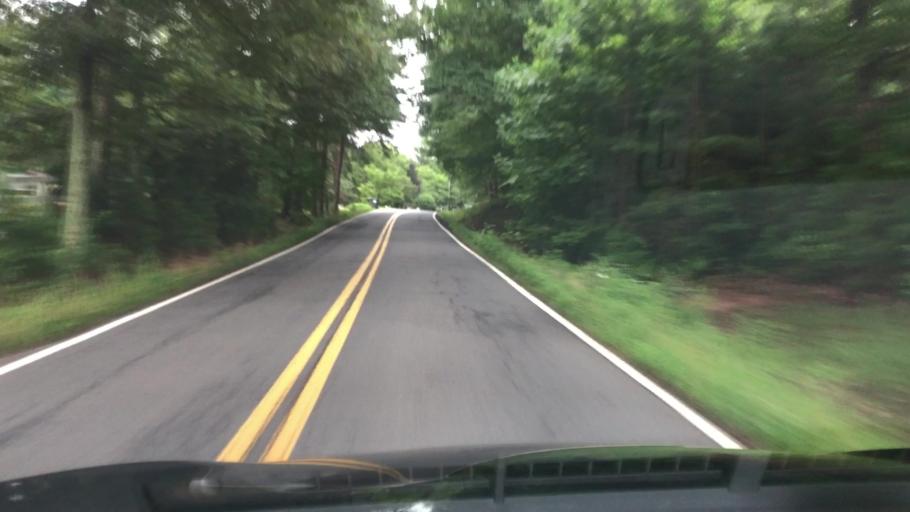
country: US
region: Virginia
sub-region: Fauquier County
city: Bealeton
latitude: 38.5084
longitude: -77.6032
